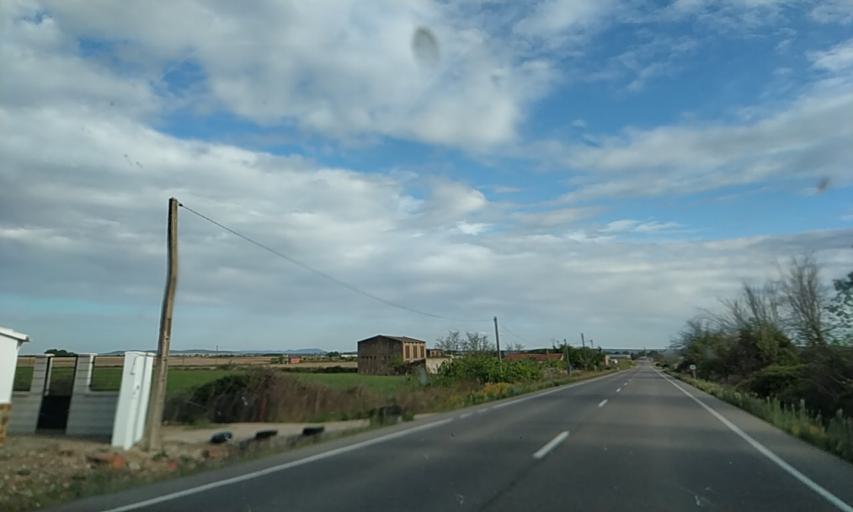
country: ES
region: Extremadura
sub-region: Provincia de Caceres
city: Moraleja
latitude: 40.0905
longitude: -6.6735
